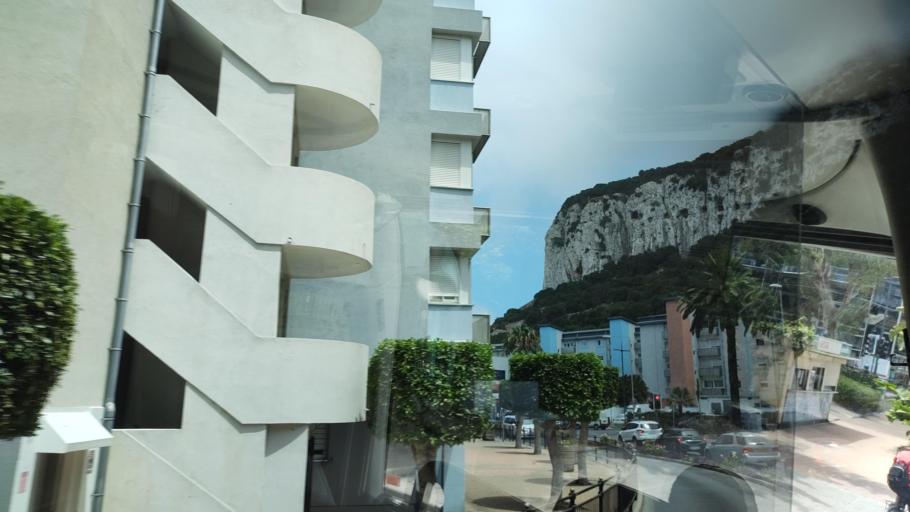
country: GI
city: Gibraltar
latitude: 36.1466
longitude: -5.3514
